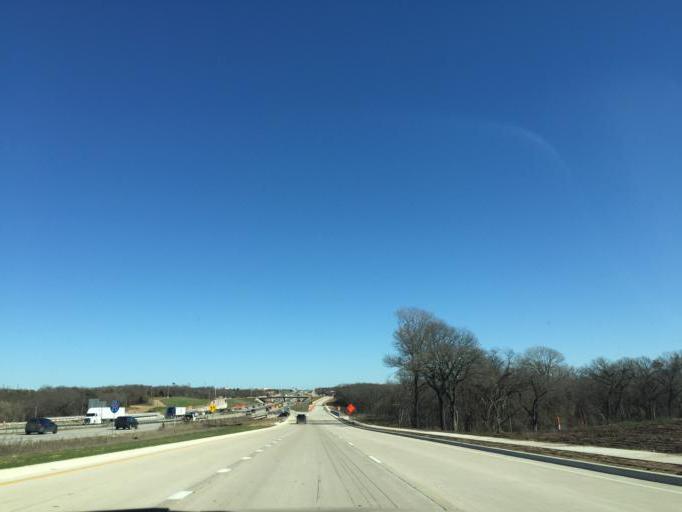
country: US
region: Texas
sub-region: Parker County
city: Hudson Oaks
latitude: 32.7455
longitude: -97.7374
